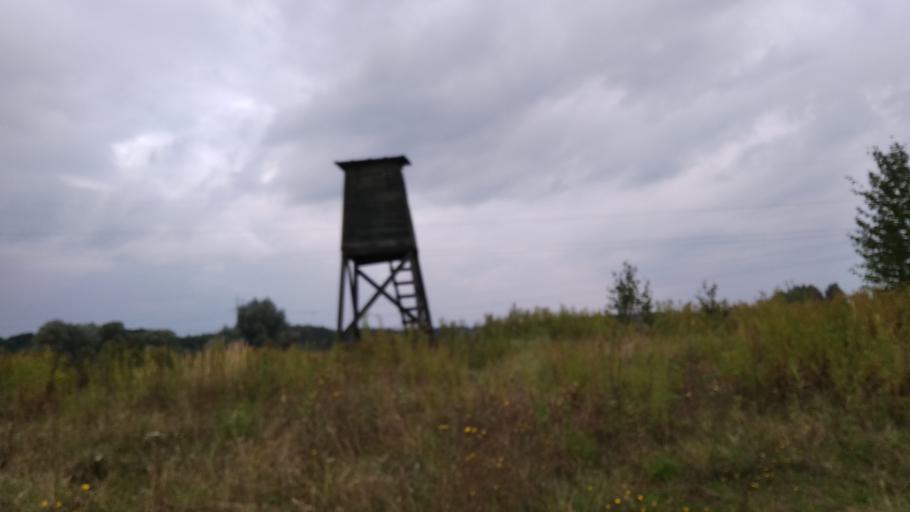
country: PL
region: Kujawsko-Pomorskie
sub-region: Powiat bydgoski
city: Osielsko
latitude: 53.2112
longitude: 18.1444
